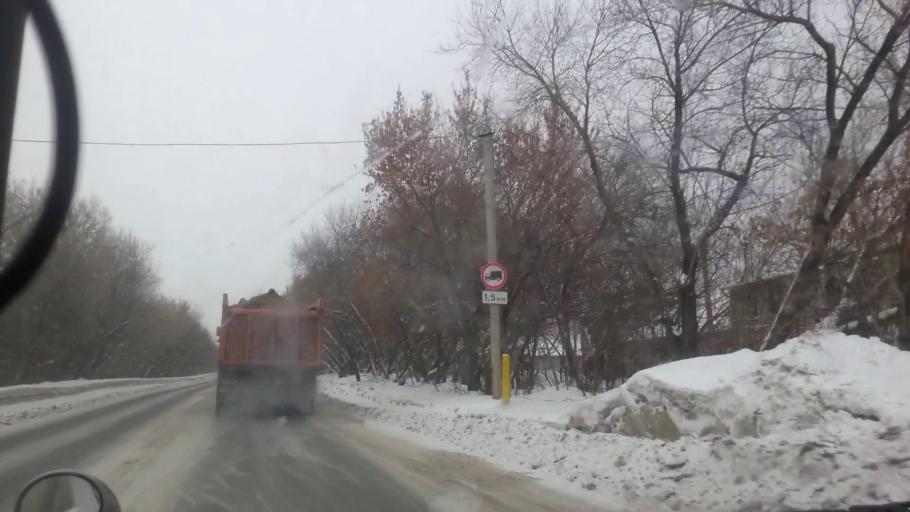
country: RU
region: Altai Krai
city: Vlasikha
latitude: 53.2996
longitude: 83.5924
